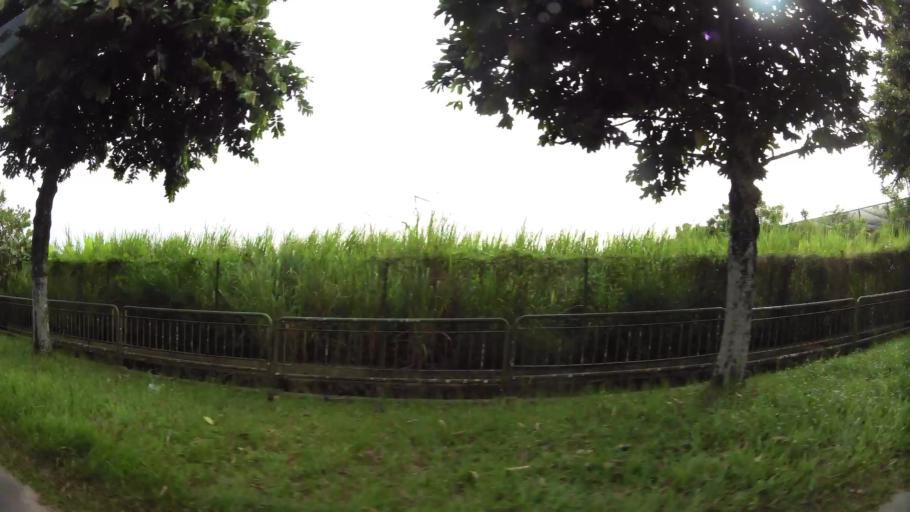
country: MY
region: Johor
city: Johor Bahru
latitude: 1.4354
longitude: 103.7114
